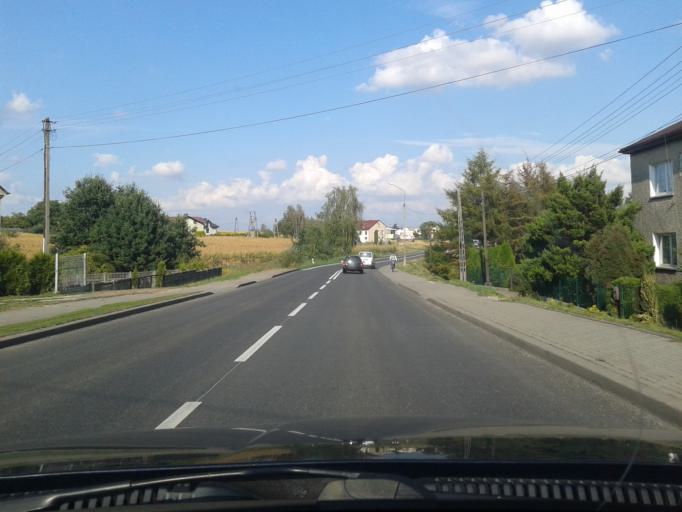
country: PL
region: Silesian Voivodeship
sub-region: Powiat wodzislawski
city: Gorzyce
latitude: 49.9611
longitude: 18.4032
